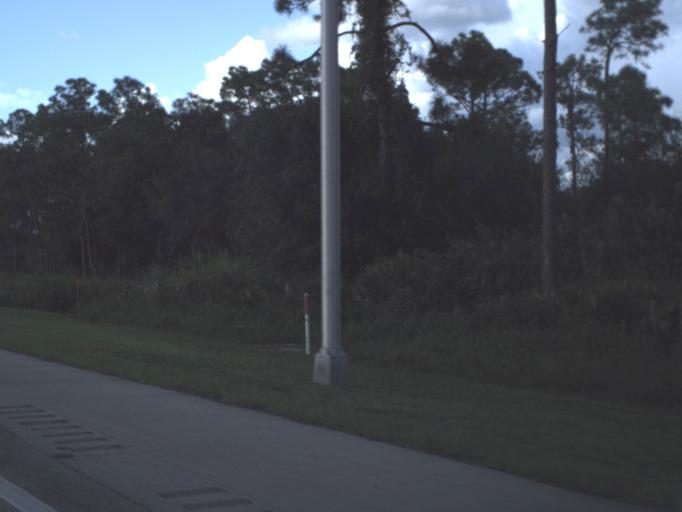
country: US
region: Florida
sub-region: Charlotte County
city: Charlotte Park
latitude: 26.8722
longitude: -81.9773
